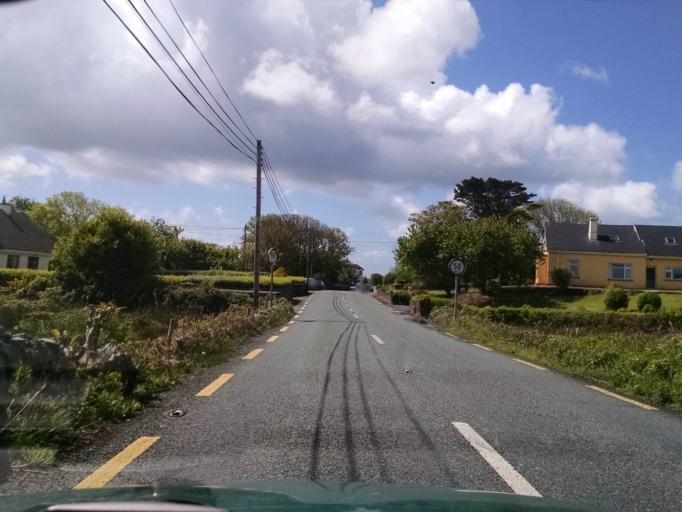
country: IE
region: Connaught
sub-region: County Galway
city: Oughterard
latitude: 53.2911
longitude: -9.6530
